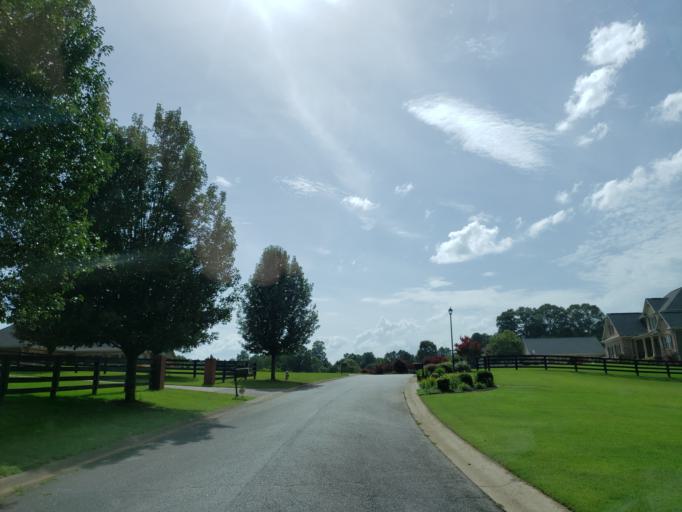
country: US
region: Georgia
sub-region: Cherokee County
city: Ball Ground
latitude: 34.3097
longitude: -84.4419
